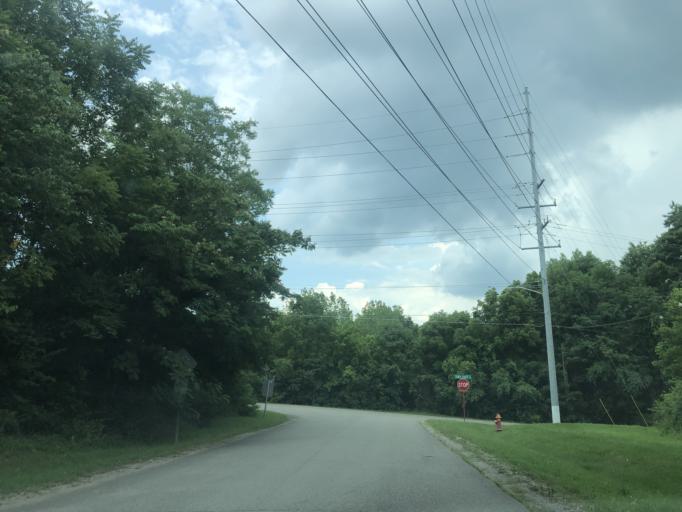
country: US
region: Tennessee
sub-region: Davidson County
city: Oak Hill
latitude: 36.1025
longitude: -86.6677
